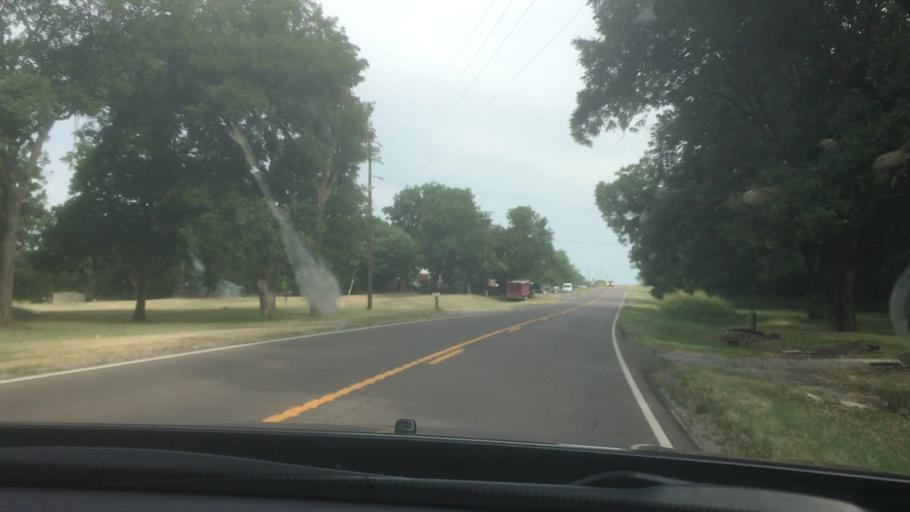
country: US
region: Oklahoma
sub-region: Garvin County
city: Pauls Valley
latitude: 34.7420
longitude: -97.2789
